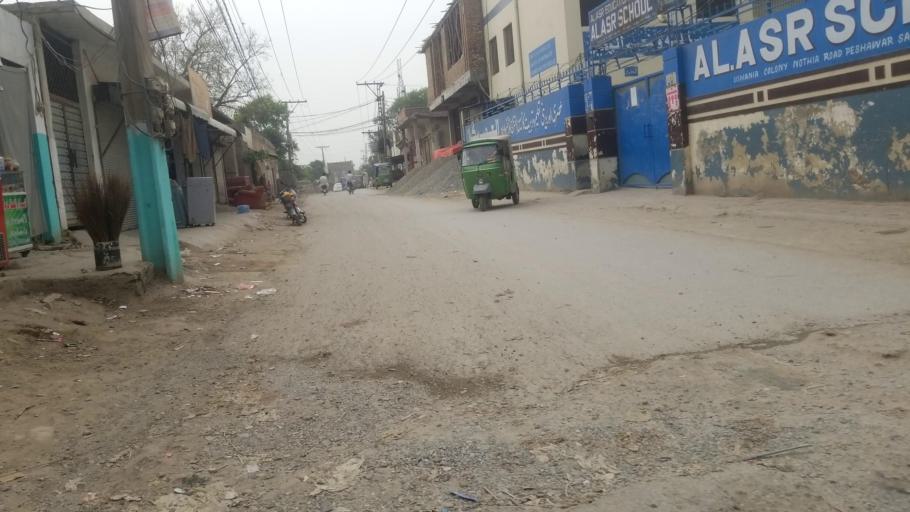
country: PK
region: Khyber Pakhtunkhwa
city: Peshawar
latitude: 33.9892
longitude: 71.5497
